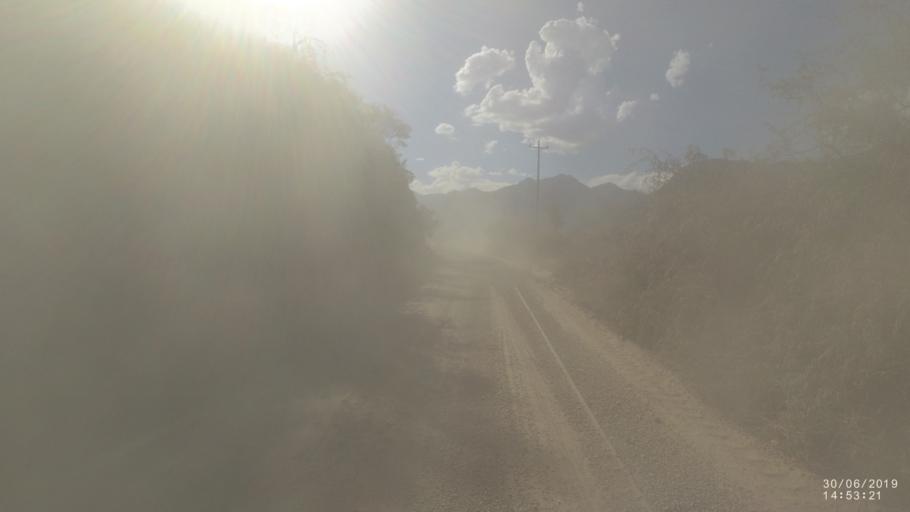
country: BO
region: Cochabamba
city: Irpa Irpa
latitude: -17.7643
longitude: -66.3482
